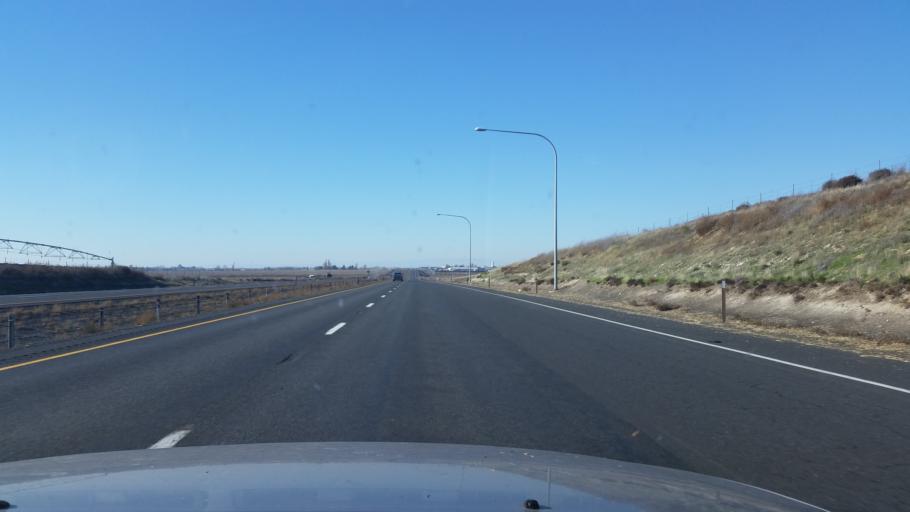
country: US
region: Washington
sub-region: Grant County
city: Moses Lake
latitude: 47.0931
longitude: -119.1783
